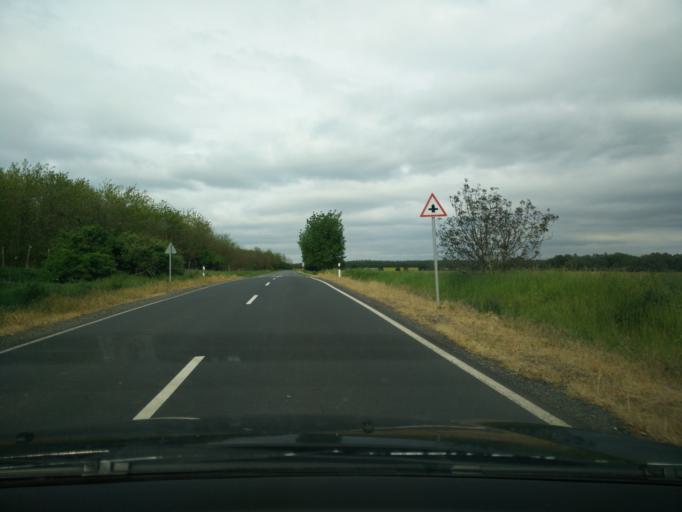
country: HU
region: Zala
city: Zalaszentgrot
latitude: 46.9932
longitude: 17.0475
